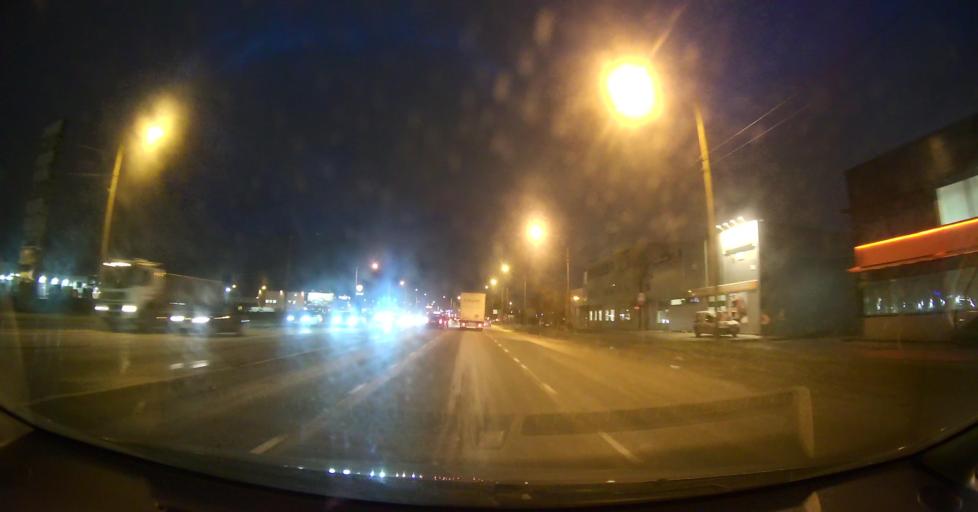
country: EE
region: Harju
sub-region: Tallinna linn
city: Kose
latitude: 59.4317
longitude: 24.8480
